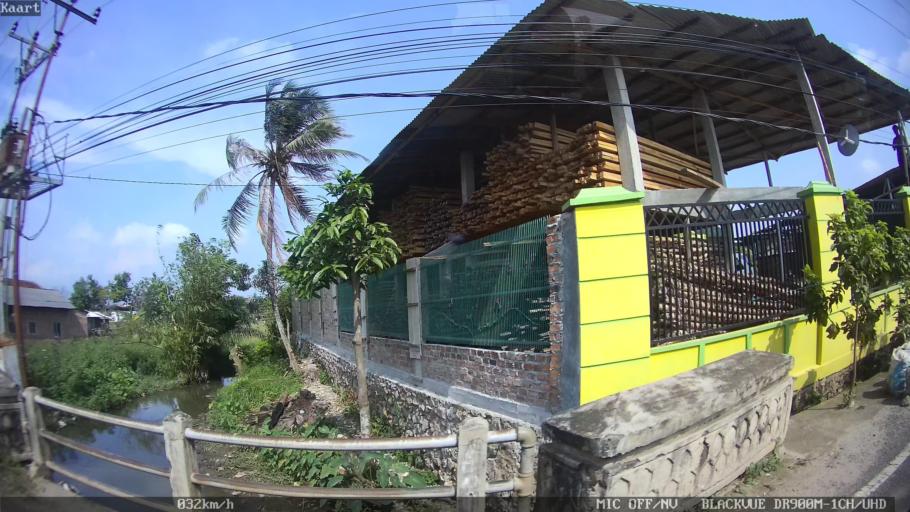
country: ID
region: Lampung
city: Kedaton
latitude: -5.3552
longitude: 105.2619
